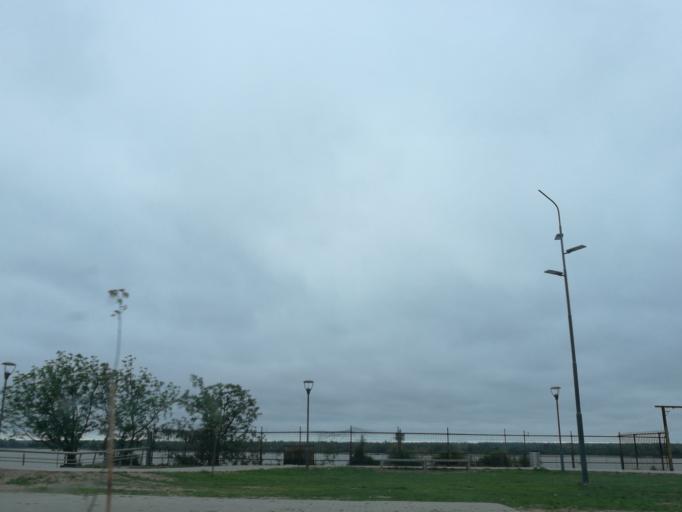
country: AR
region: Santa Fe
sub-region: Departamento de Rosario
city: Rosario
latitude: -32.9280
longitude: -60.6559
